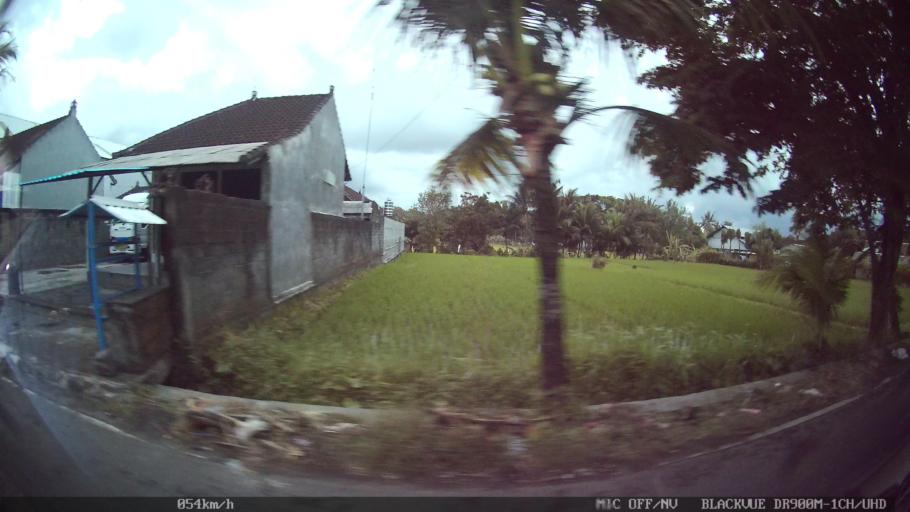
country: ID
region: Bali
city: Banjar Serangan
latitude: -8.5560
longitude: 115.1802
